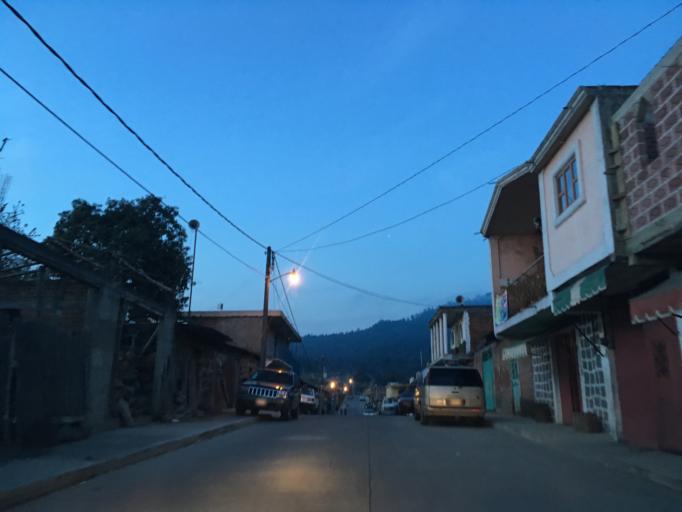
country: MX
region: Michoacan
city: Charapan
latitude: 19.6946
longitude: -102.1898
